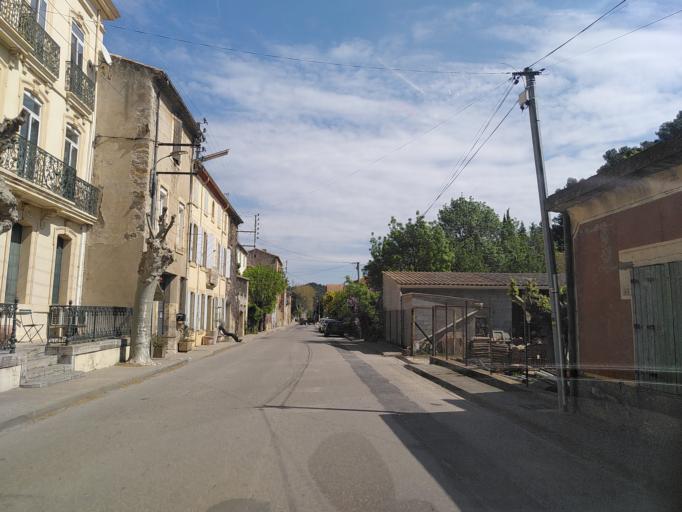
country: FR
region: Languedoc-Roussillon
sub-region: Departement de l'Aude
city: Portel-des-Corbieres
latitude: 42.9966
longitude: 2.8174
